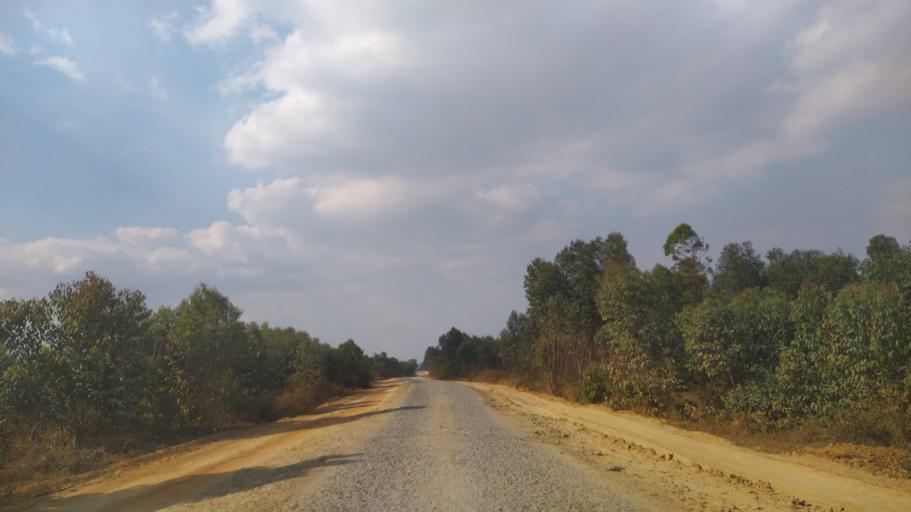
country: MG
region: Alaotra Mangoro
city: Moramanga
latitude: -18.6436
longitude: 48.2755
